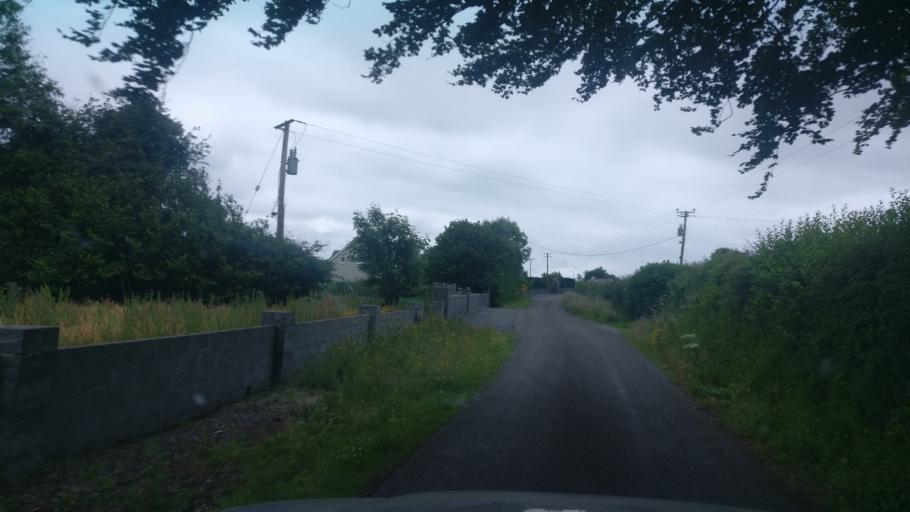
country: IE
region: Connaught
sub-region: County Galway
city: Ballinasloe
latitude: 53.2934
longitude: -8.3400
